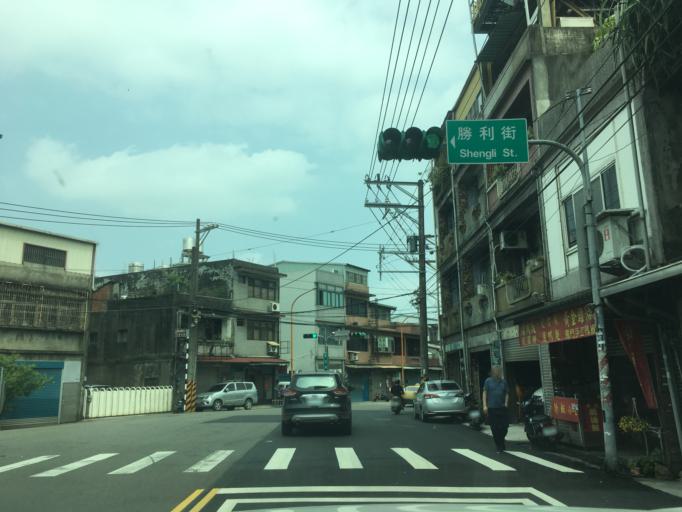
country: TW
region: Taiwan
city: Daxi
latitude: 24.8755
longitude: 121.2866
